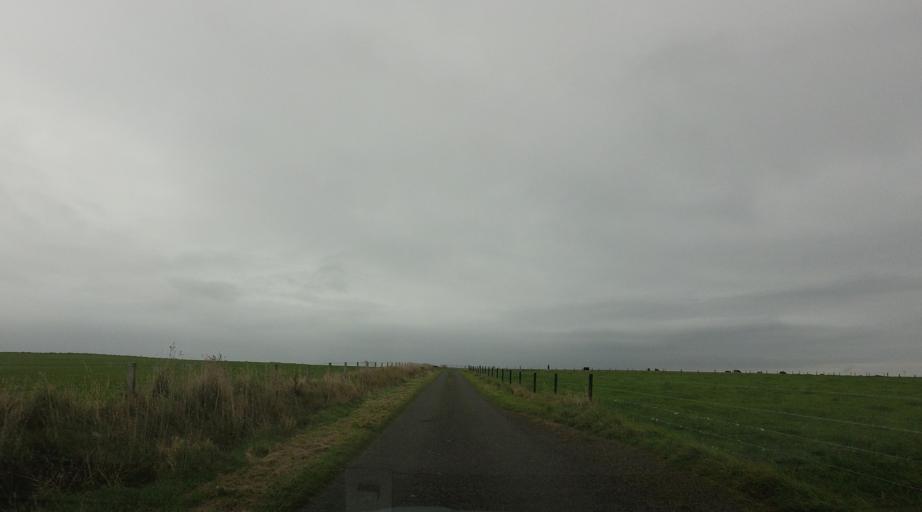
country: GB
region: Scotland
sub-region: Orkney Islands
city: Orkney
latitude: 58.7375
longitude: -2.9613
